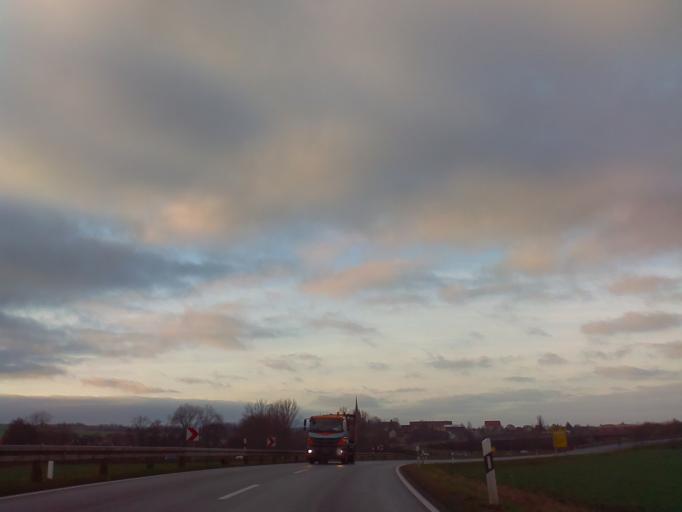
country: DE
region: Thuringia
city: Neustadt (Orla)
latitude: 50.7331
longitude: 11.7276
